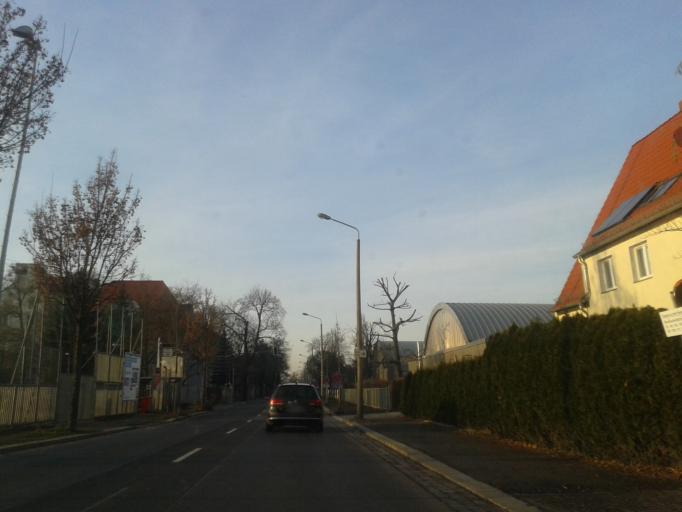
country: DE
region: Saxony
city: Heidenau
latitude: 51.0085
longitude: 13.8168
